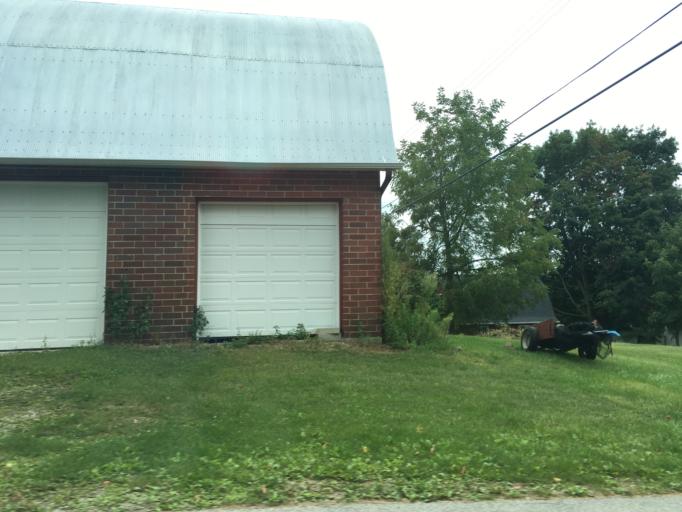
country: US
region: Michigan
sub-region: Lapeer County
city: Barnes Lake-Millers Lake
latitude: 43.3365
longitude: -83.3453
